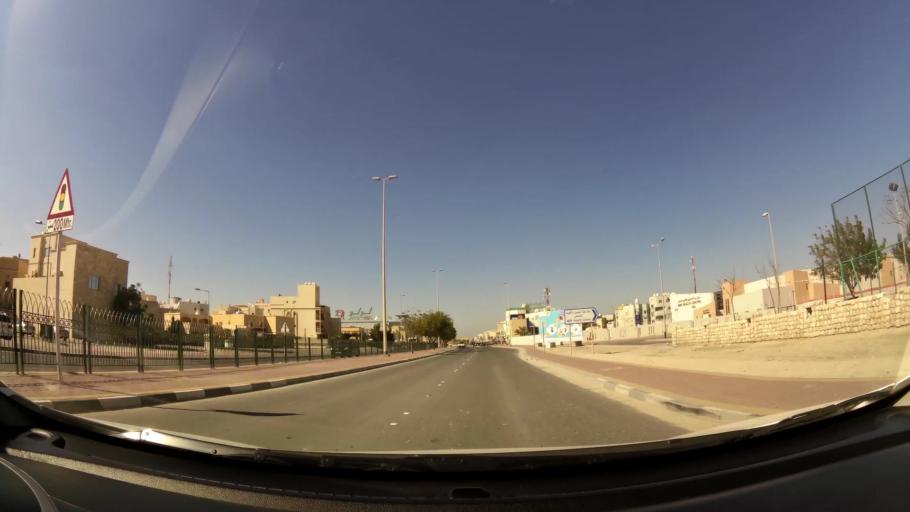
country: BH
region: Muharraq
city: Al Hadd
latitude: 26.2352
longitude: 50.6522
